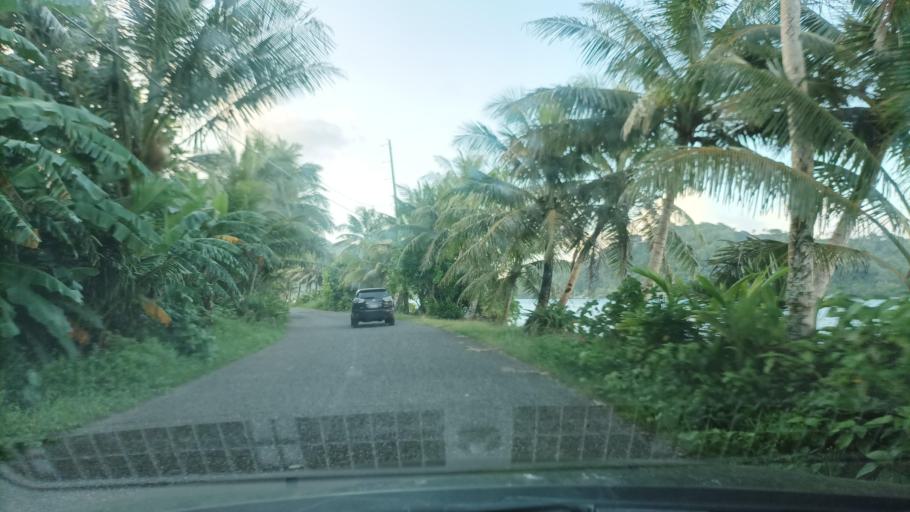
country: FM
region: Kosrae
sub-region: Lelu Municipality
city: Lelu
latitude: 5.3200
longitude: 163.0322
